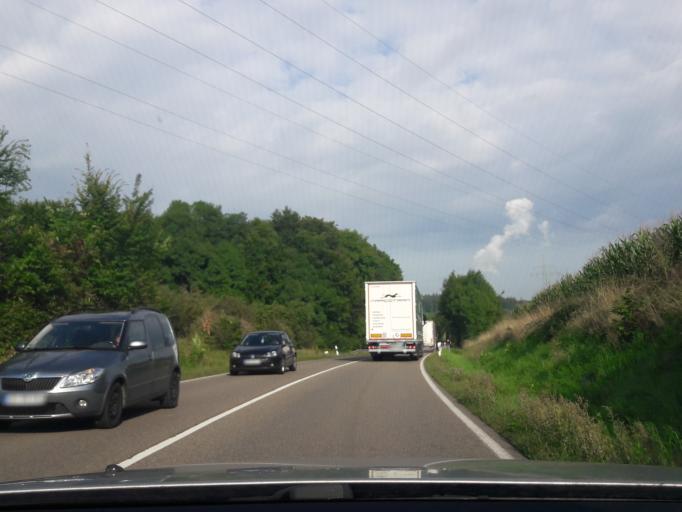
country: DE
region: Baden-Wuerttemberg
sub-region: Regierungsbezirk Stuttgart
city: Grossbottwar
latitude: 49.0060
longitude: 9.2566
